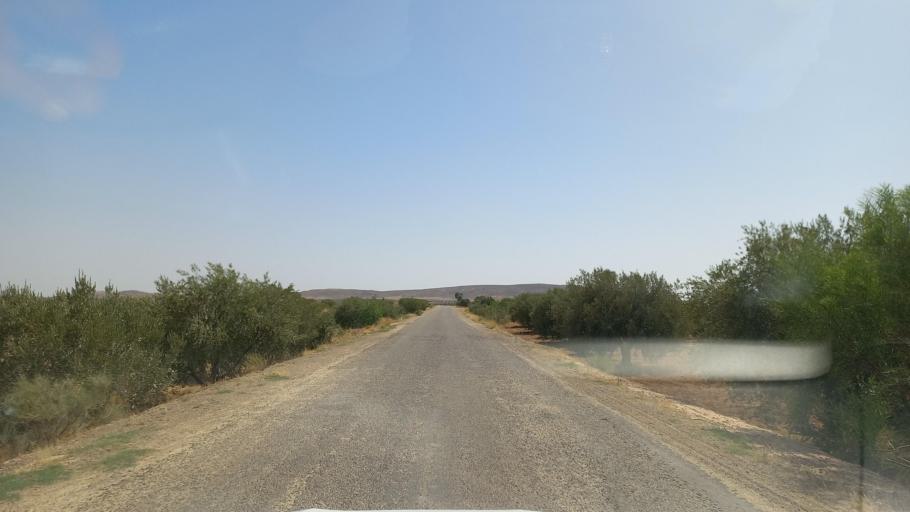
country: TN
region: Al Qasrayn
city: Kasserine
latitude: 35.2150
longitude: 9.0417
